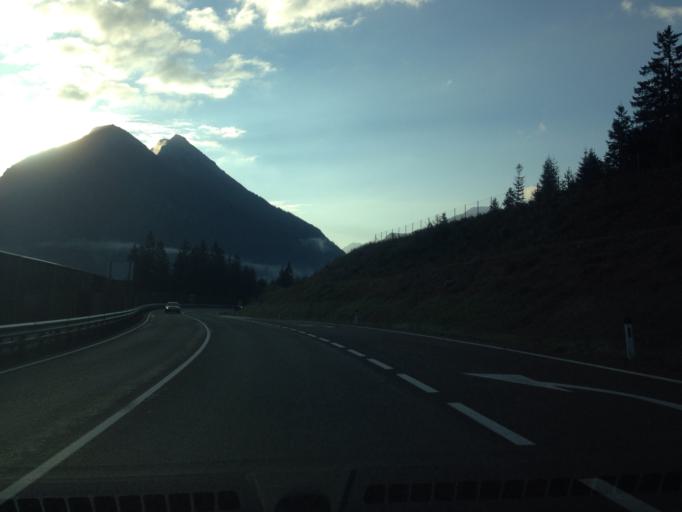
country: AT
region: Tyrol
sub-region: Politischer Bezirk Reutte
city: Heiterwang
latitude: 47.4477
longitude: 10.7346
